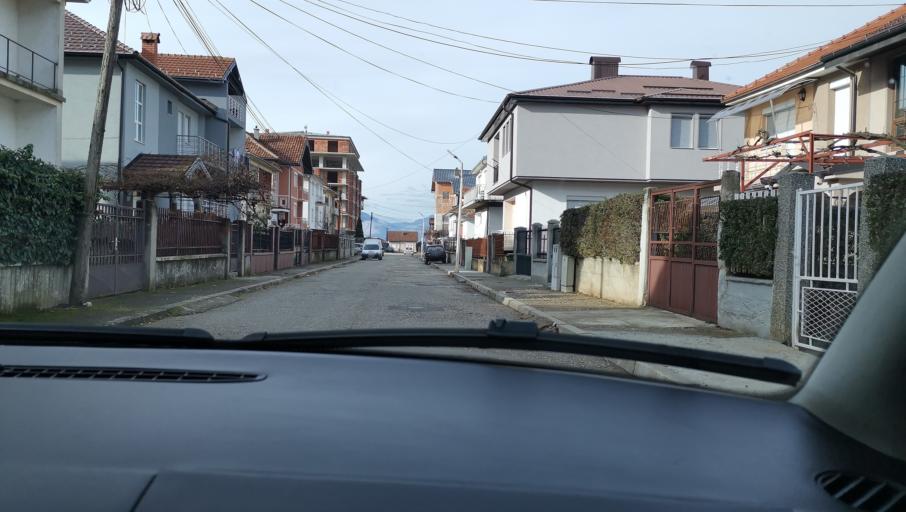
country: MK
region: Debar
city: Debar
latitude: 41.5153
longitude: 20.5289
